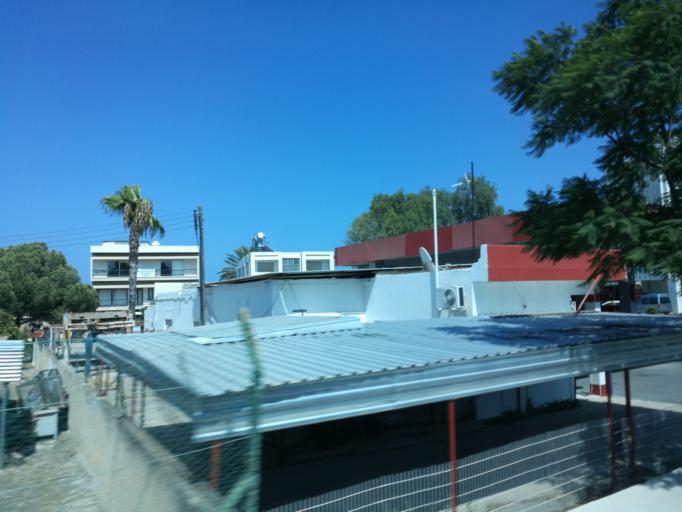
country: CY
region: Ammochostos
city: Famagusta
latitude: 35.1162
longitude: 33.9446
